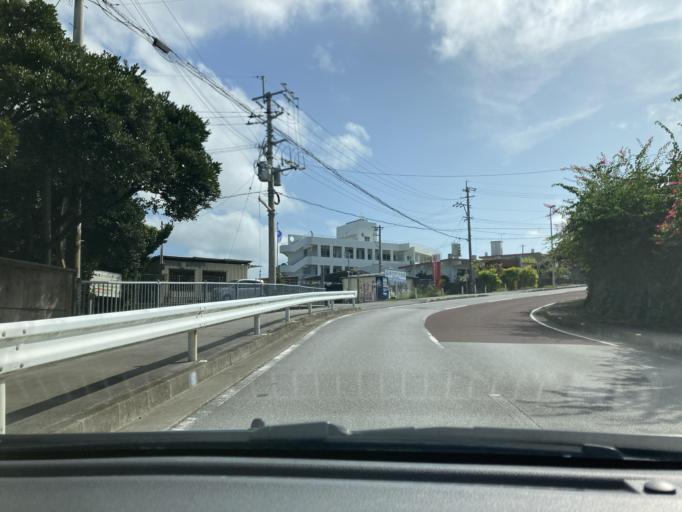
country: JP
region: Okinawa
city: Chatan
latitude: 26.2947
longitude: 127.7947
